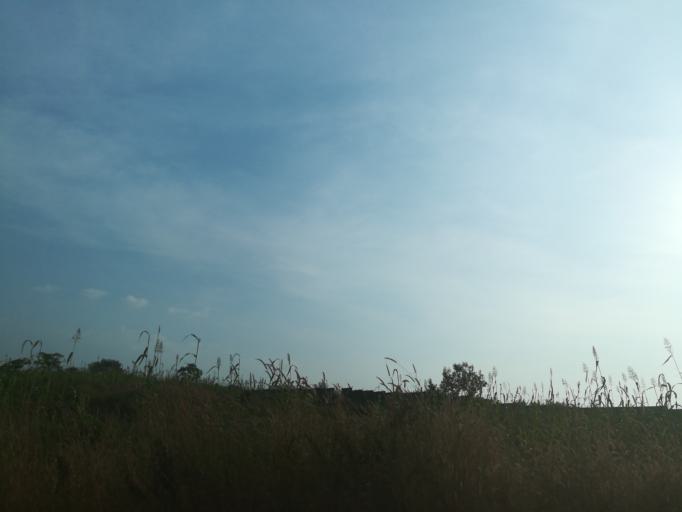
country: NG
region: Abuja Federal Capital Territory
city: Abuja
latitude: 9.0909
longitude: 7.3713
